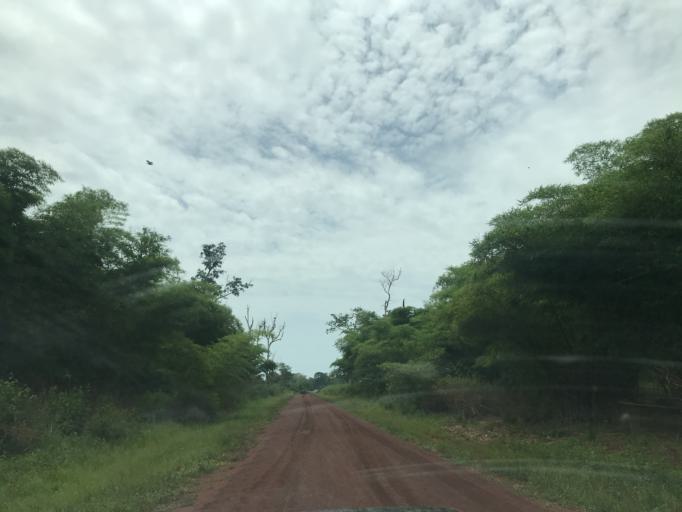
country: CD
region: Eastern Province
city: Buta
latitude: 2.4107
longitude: 24.8980
